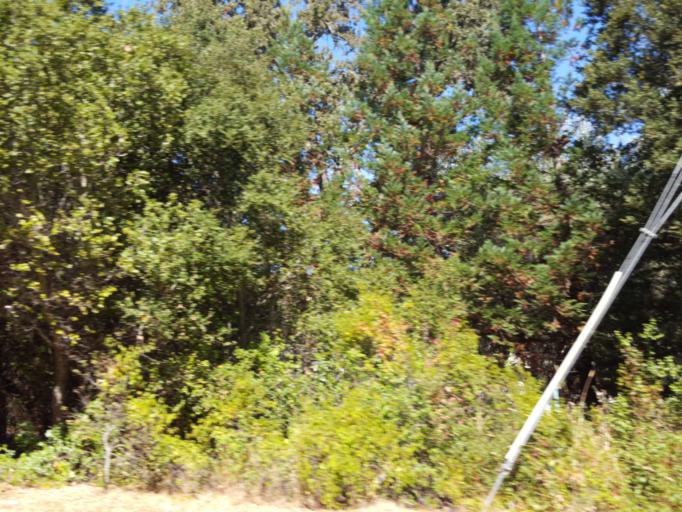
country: US
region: California
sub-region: San Mateo County
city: Ladera
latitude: 37.3742
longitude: -122.2043
